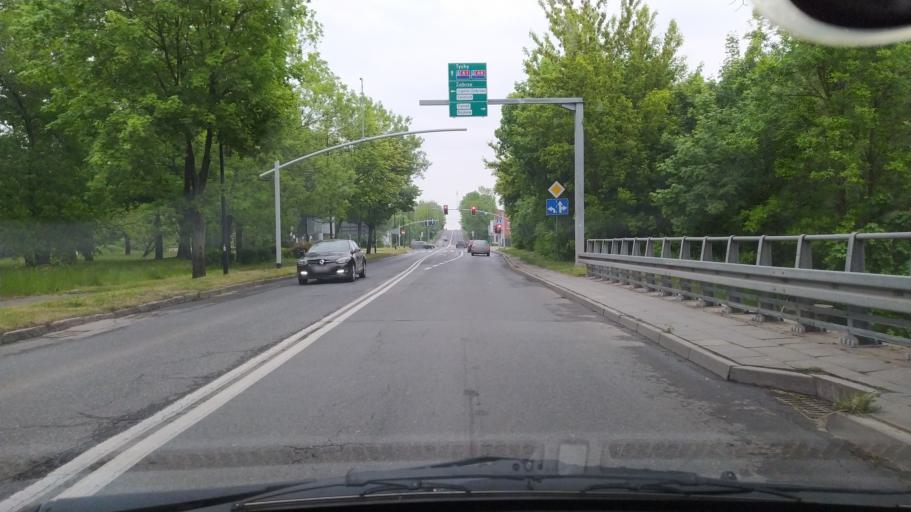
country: PL
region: Silesian Voivodeship
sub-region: Gliwice
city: Gliwice
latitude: 50.2739
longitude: 18.7007
